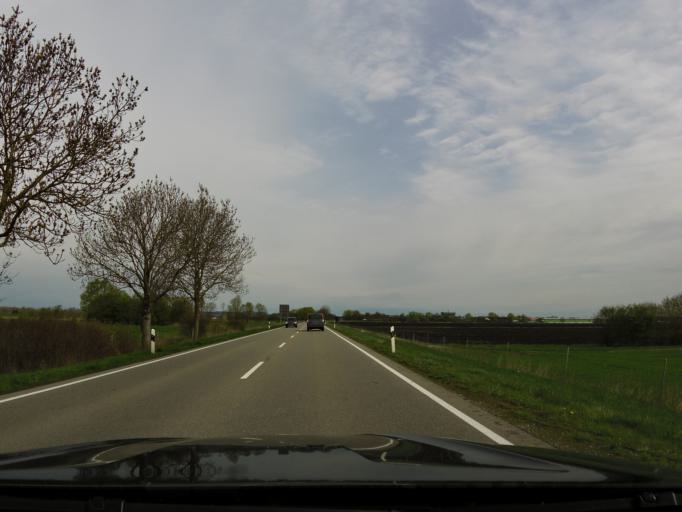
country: DE
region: Bavaria
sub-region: Upper Bavaria
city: Eitting
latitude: 48.3637
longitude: 11.8530
